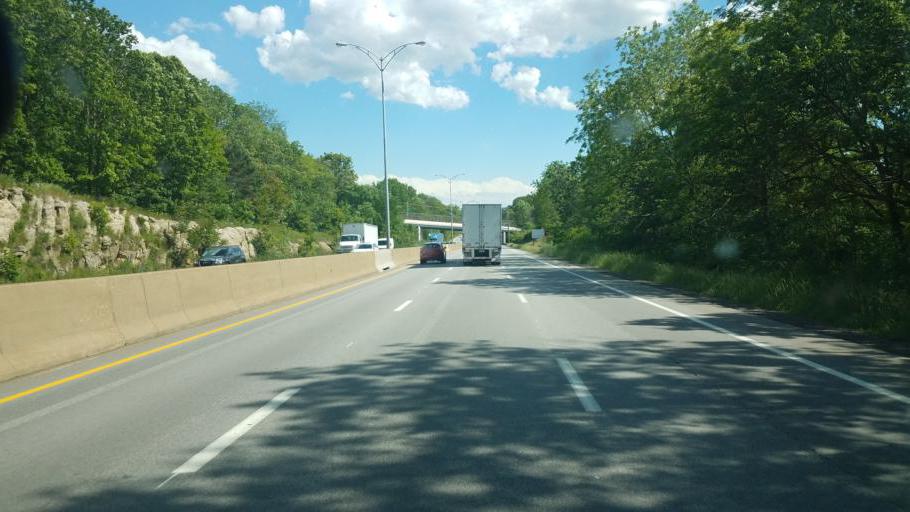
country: US
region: Ohio
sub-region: Summit County
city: Akron
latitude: 41.0542
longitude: -81.5666
